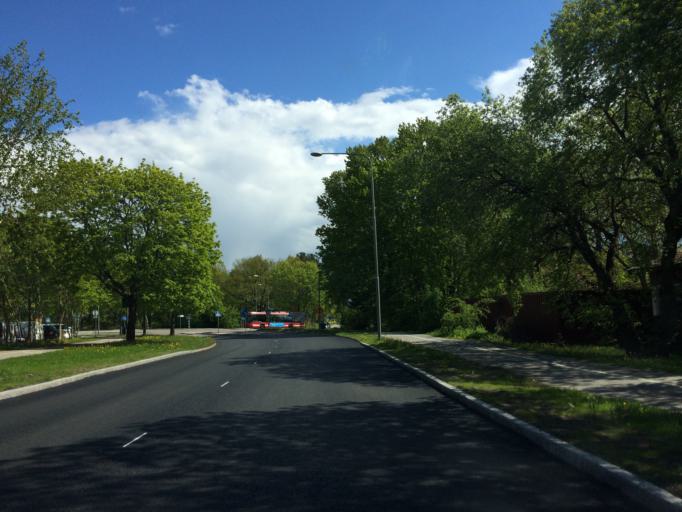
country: SE
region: Stockholm
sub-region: Huddinge Kommun
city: Segeltorp
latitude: 59.2821
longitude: 17.9631
